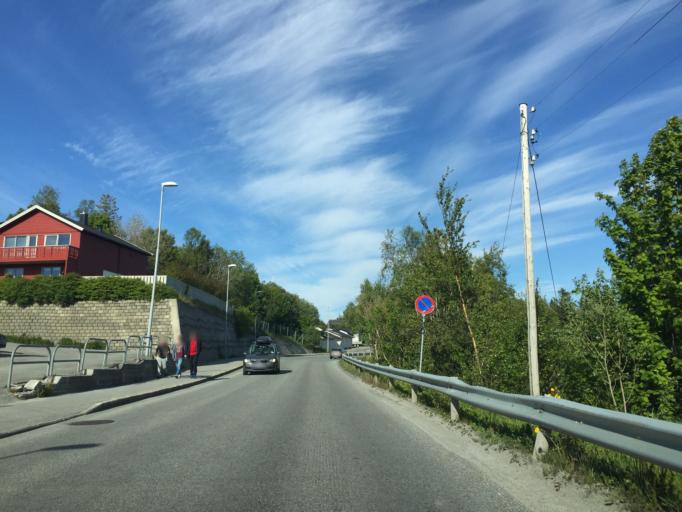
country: NO
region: Nordland
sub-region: Bodo
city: Lopsmarka
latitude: 67.2825
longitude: 14.5459
